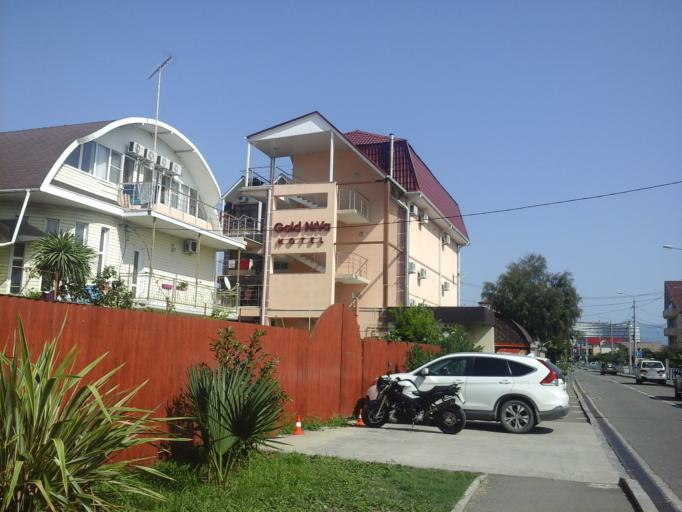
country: RU
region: Krasnodarskiy
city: Adler
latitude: 43.4143
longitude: 39.9561
